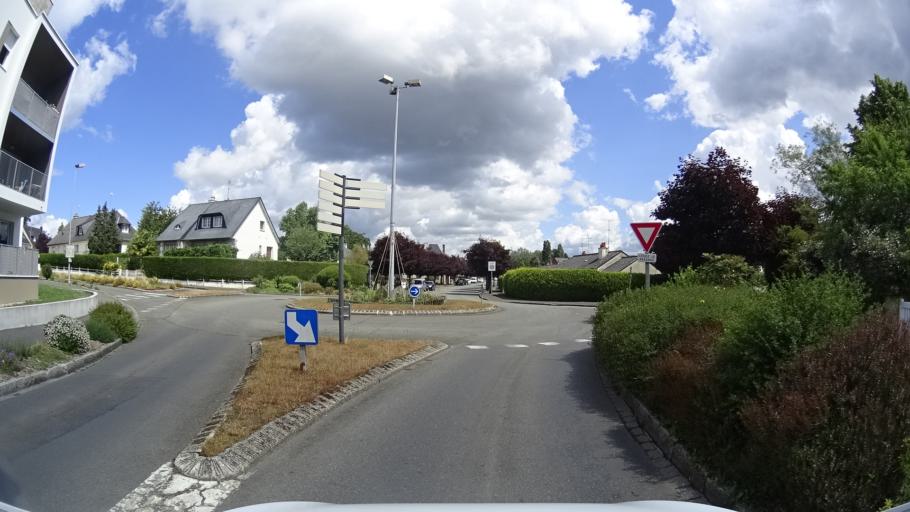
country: FR
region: Brittany
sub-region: Departement d'Ille-et-Vilaine
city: Chartres-de-Bretagne
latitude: 48.0374
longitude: -1.7063
